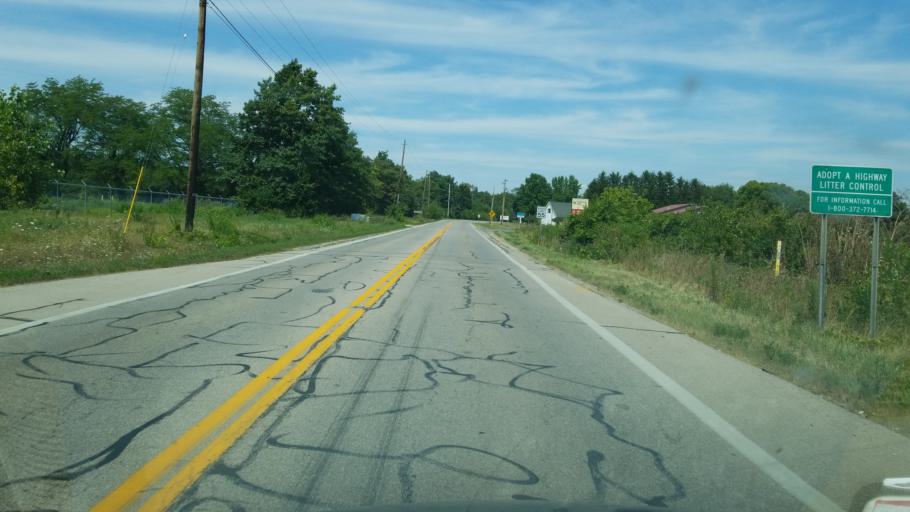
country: US
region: Ohio
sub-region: Madison County
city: Plain City
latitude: 40.1247
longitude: -83.2719
